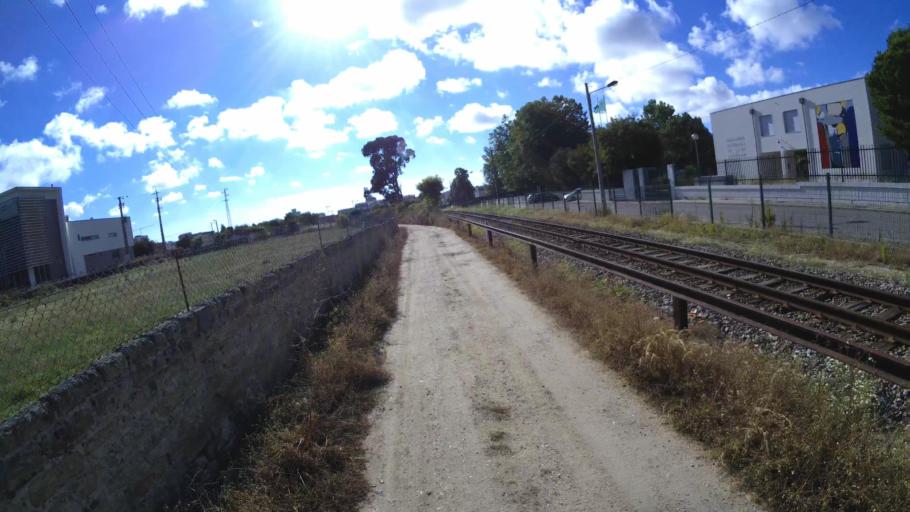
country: PT
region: Aveiro
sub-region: Aveiro
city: Aveiro
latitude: 40.6442
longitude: -8.6320
